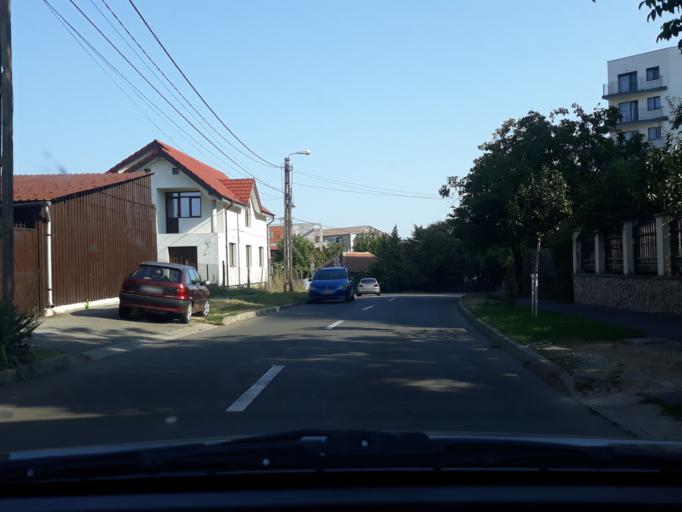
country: RO
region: Bihor
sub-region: Comuna Biharea
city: Oradea
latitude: 47.0358
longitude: 21.9397
